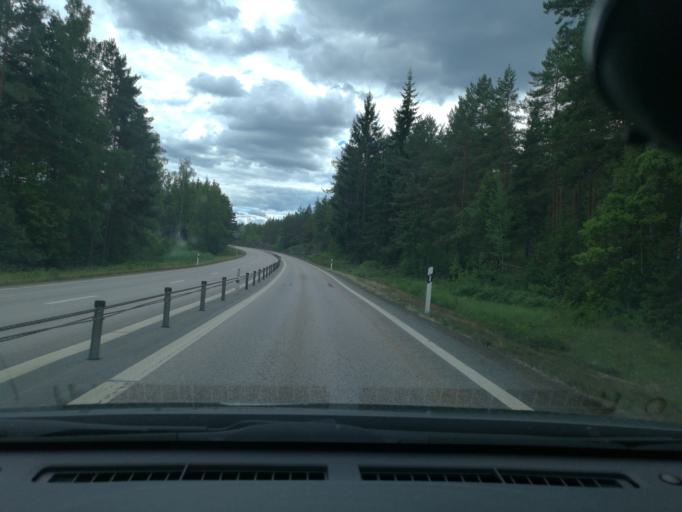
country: SE
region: Kalmar
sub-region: Vasterviks Kommun
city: Forserum
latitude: 58.0354
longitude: 16.5161
